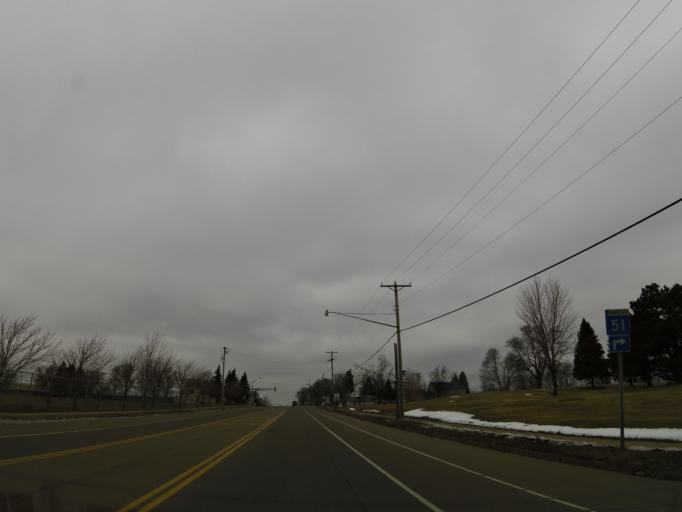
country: US
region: Minnesota
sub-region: Dakota County
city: Mendota Heights
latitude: 44.9126
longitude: -93.1645
